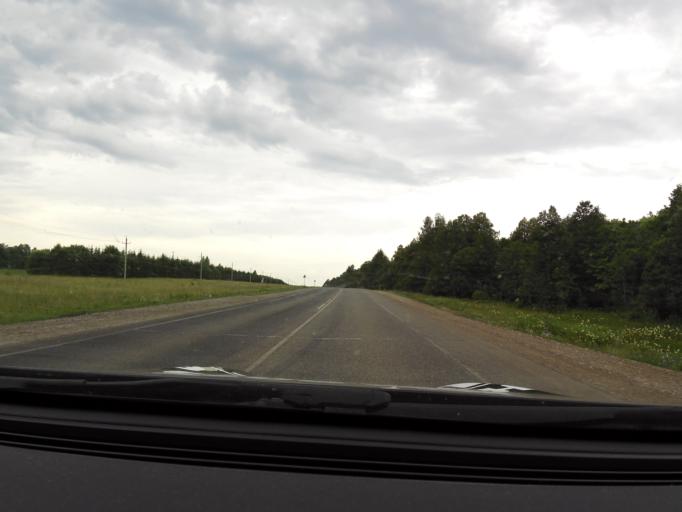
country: RU
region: Bashkortostan
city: Kudeyevskiy
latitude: 54.8082
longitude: 56.6369
